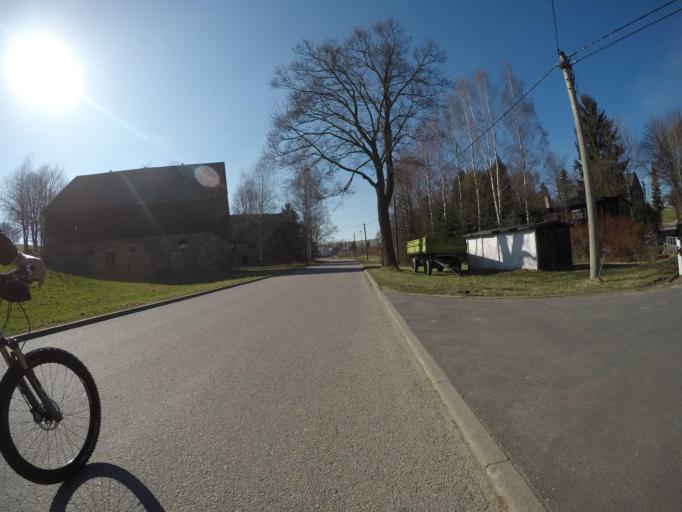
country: DE
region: Saxony
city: Lichtenberg
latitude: 50.8388
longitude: 13.3902
